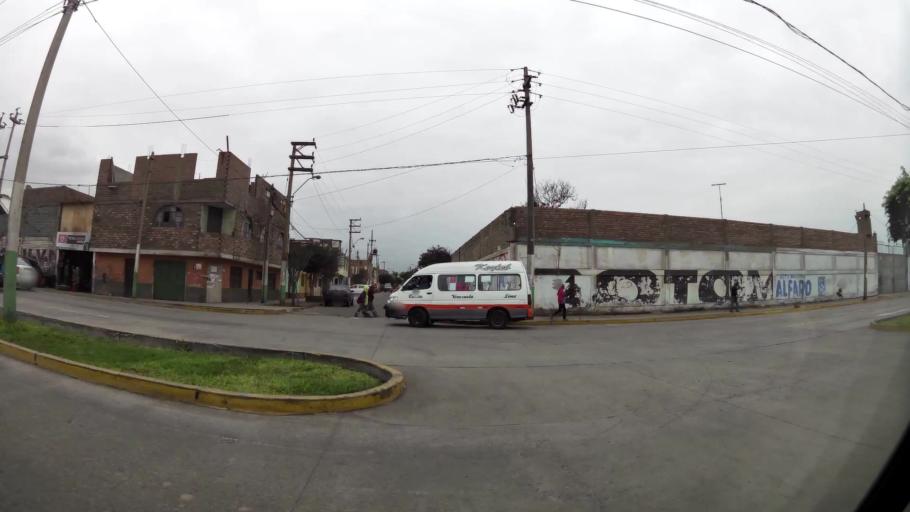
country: PE
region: Callao
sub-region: Callao
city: Callao
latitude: -12.0482
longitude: -77.1347
